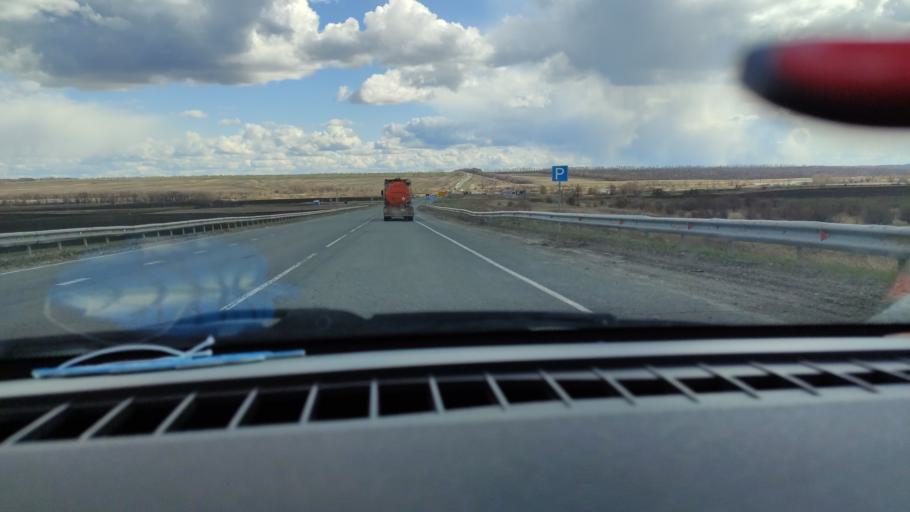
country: RU
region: Saratov
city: Dukhovnitskoye
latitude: 52.7443
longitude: 48.2522
